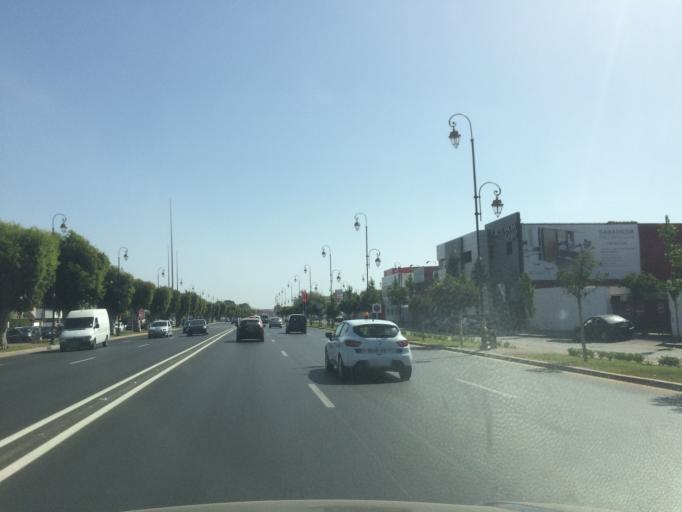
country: MA
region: Rabat-Sale-Zemmour-Zaer
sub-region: Rabat
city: Rabat
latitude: 33.9811
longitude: -6.8735
